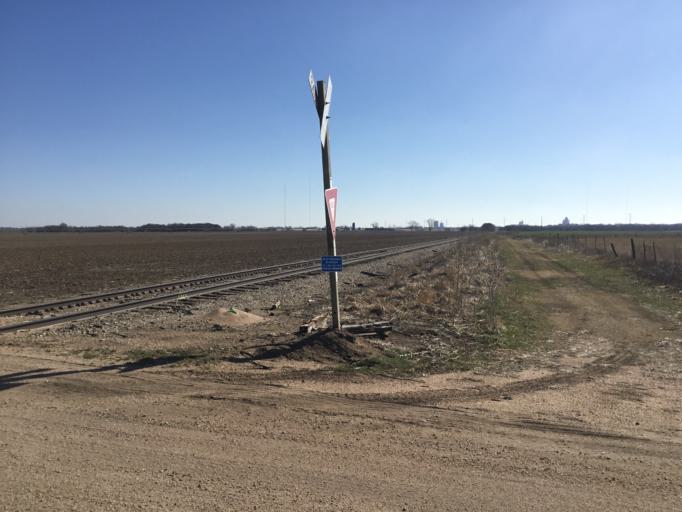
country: US
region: Kansas
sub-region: Sedgwick County
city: Colwich
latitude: 37.7862
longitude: -97.5727
